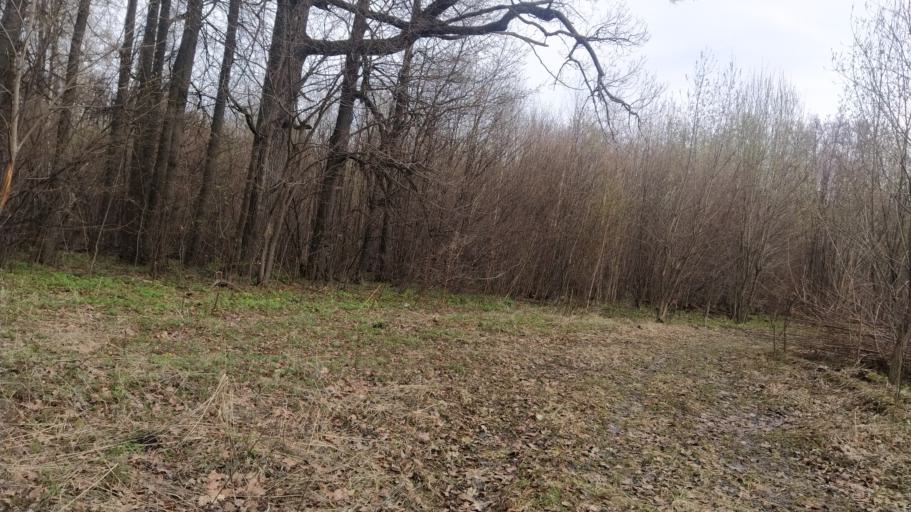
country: RU
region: Chuvashia
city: Novyye Lapsary
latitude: 56.1395
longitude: 47.1234
